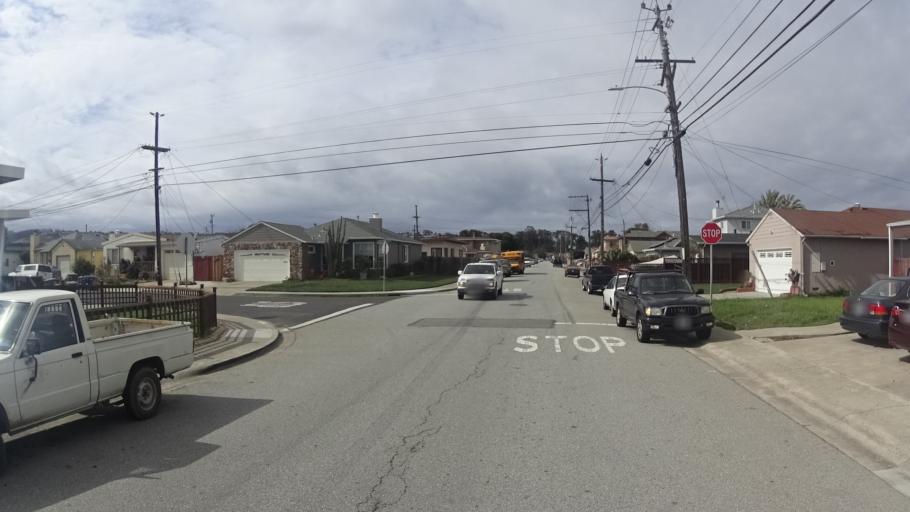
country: US
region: California
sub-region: San Mateo County
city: South San Francisco
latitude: 37.6515
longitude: -122.4204
